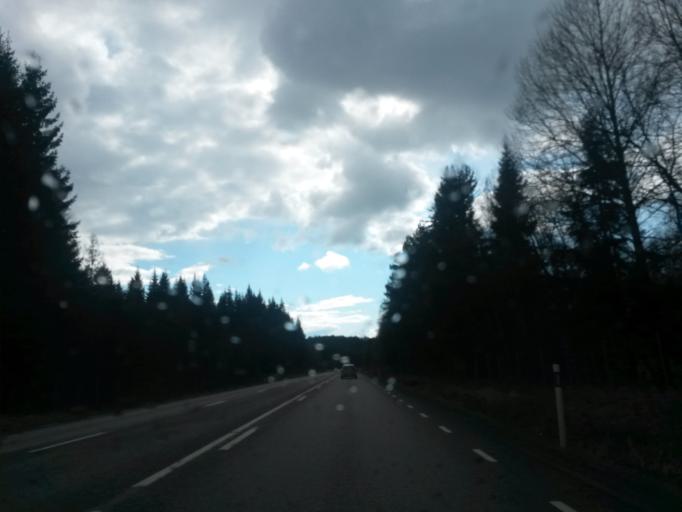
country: SE
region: Vaestra Goetaland
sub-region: Skovde Kommun
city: Skultorp
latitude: 58.3805
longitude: 13.7258
